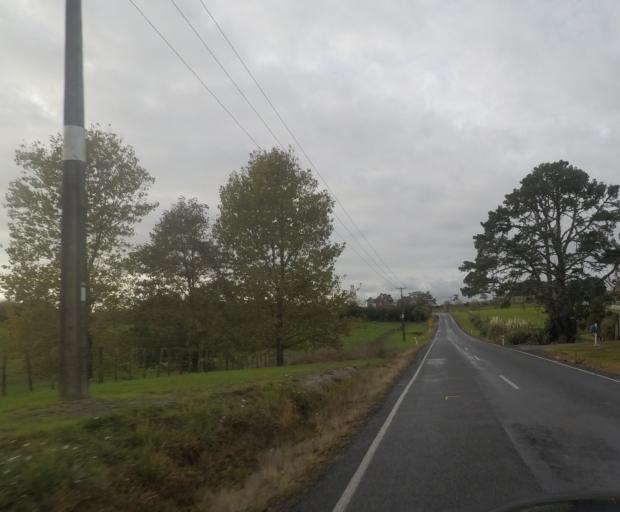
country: NZ
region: Auckland
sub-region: Auckland
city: Wellsford
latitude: -36.2213
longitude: 174.5697
